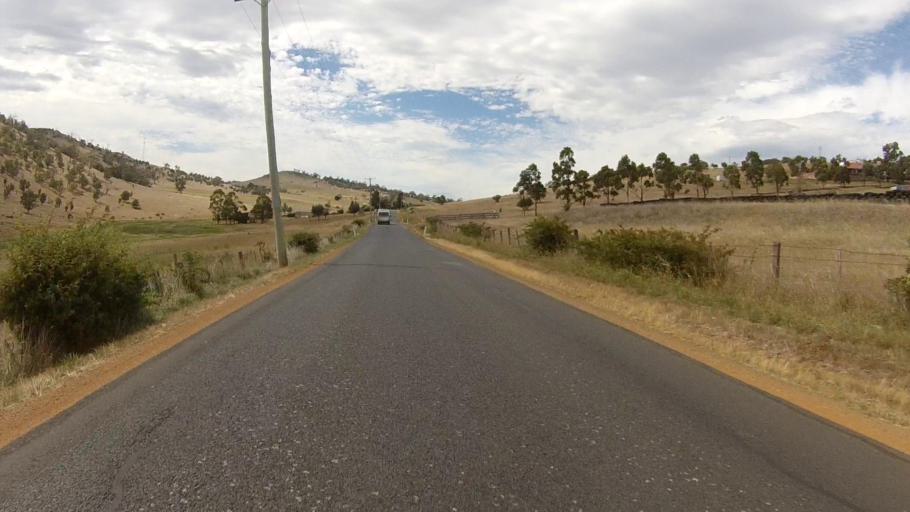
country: AU
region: Tasmania
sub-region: Brighton
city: Bridgewater
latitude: -42.6995
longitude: 147.3049
